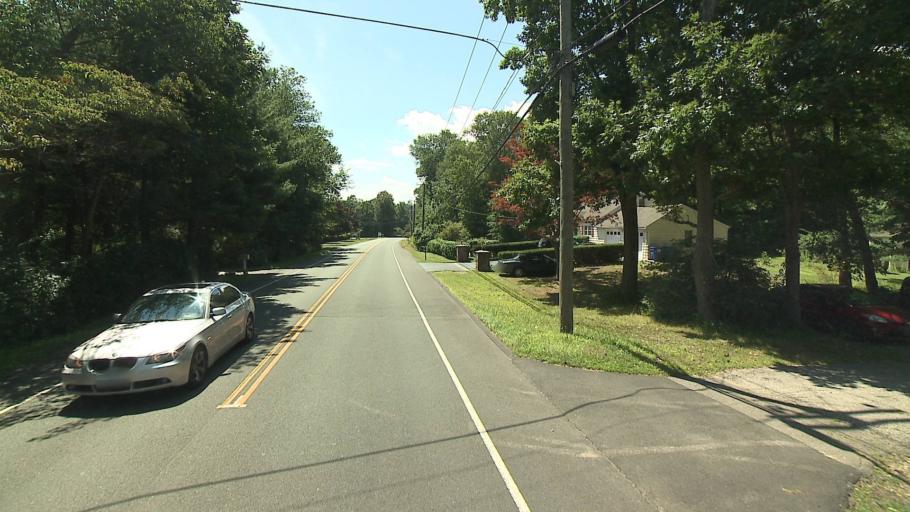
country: US
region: Connecticut
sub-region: Fairfield County
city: Trumbull
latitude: 41.3225
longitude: -73.2113
